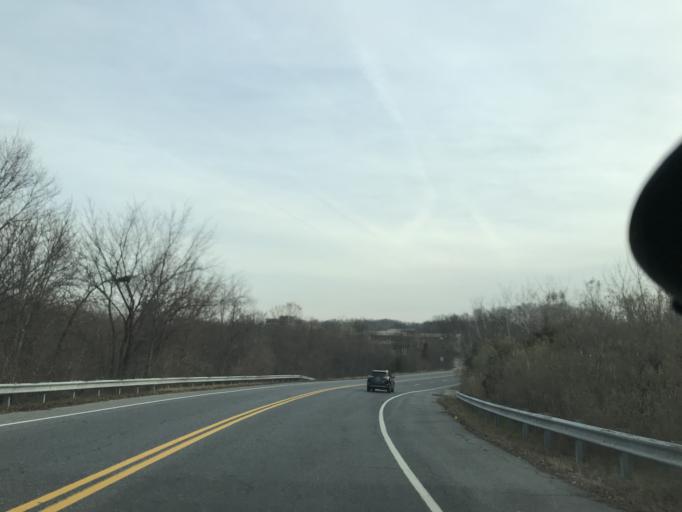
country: US
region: Maryland
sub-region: Prince George's County
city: Glenarden
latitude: 38.9454
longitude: -76.8697
